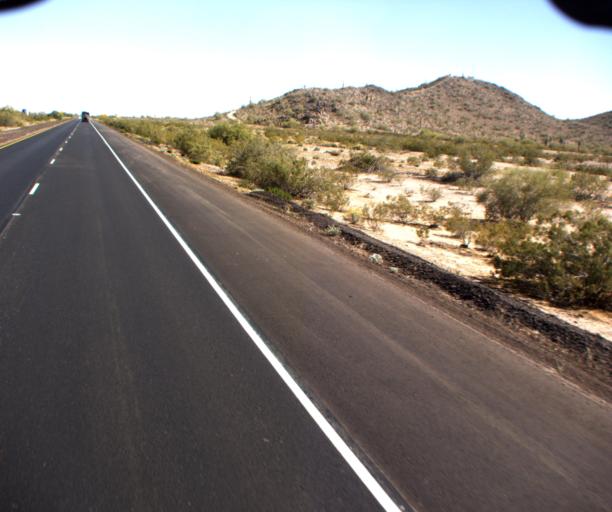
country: US
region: Arizona
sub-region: Pinal County
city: Casa Grande
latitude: 32.8308
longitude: -111.7062
